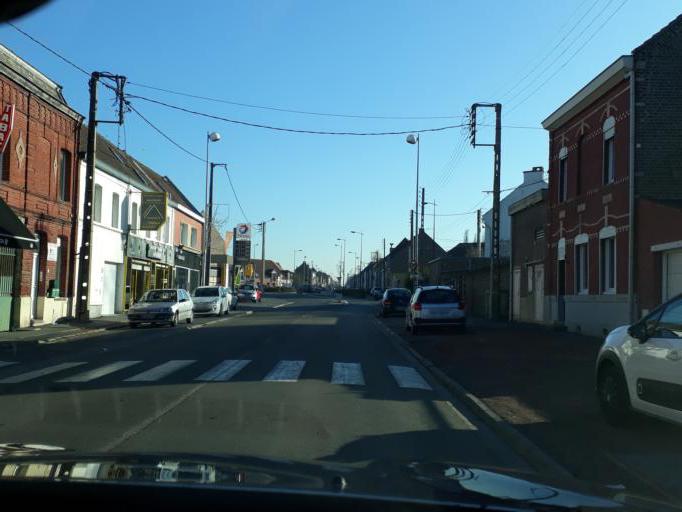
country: FR
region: Nord-Pas-de-Calais
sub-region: Departement du Nord
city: Auberchicourt
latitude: 50.3305
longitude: 3.2421
